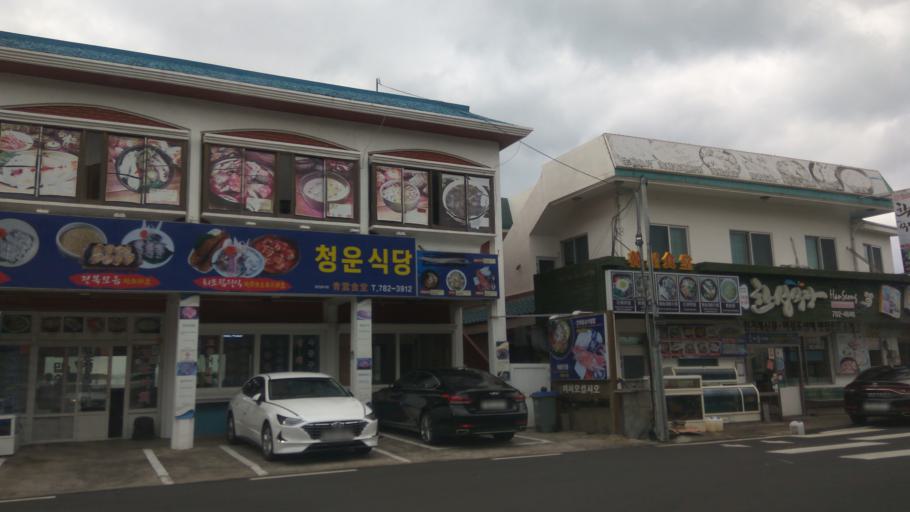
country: KR
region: Jeju-do
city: Jeju-si
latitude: 33.4629
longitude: 126.9351
